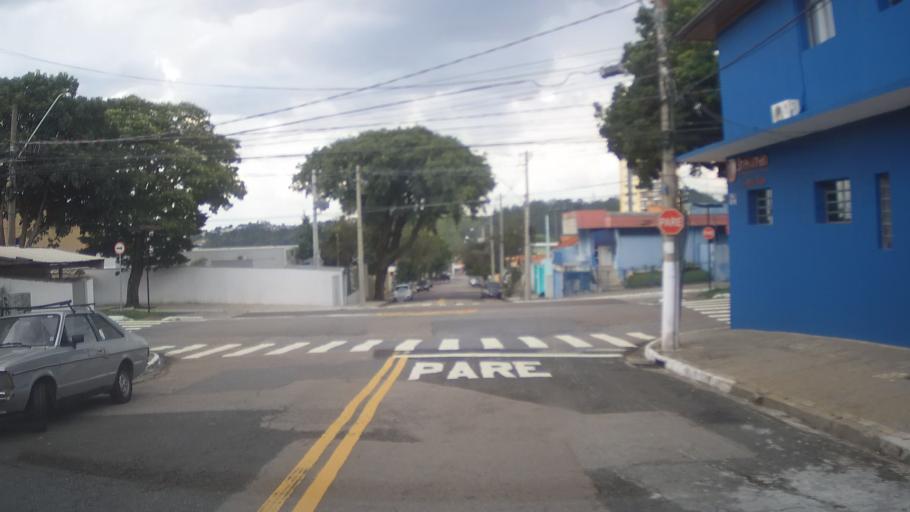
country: BR
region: Sao Paulo
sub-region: Jundiai
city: Jundiai
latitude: -23.2073
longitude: -46.8683
